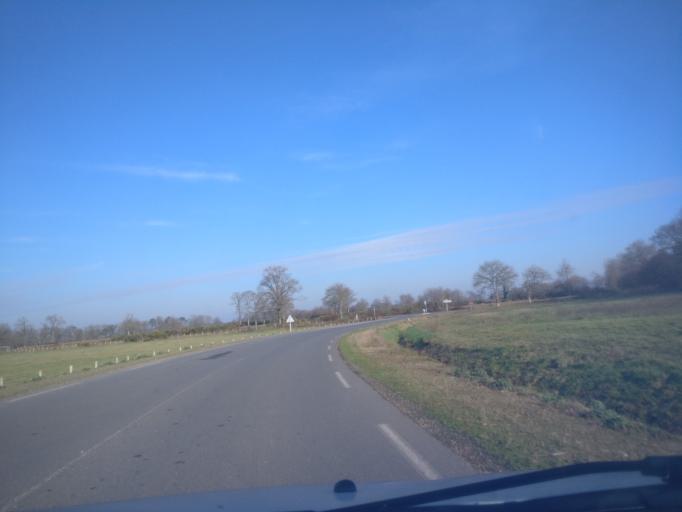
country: FR
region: Brittany
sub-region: Departement d'Ille-et-Vilaine
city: Livre-sur-Changeon
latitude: 48.2425
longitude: -1.3657
